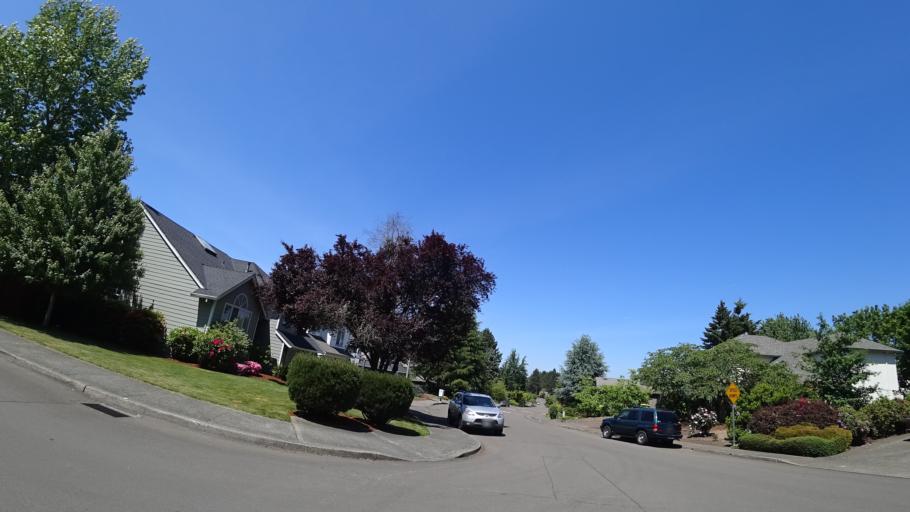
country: US
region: Oregon
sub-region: Washington County
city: King City
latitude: 45.4308
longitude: -122.8134
